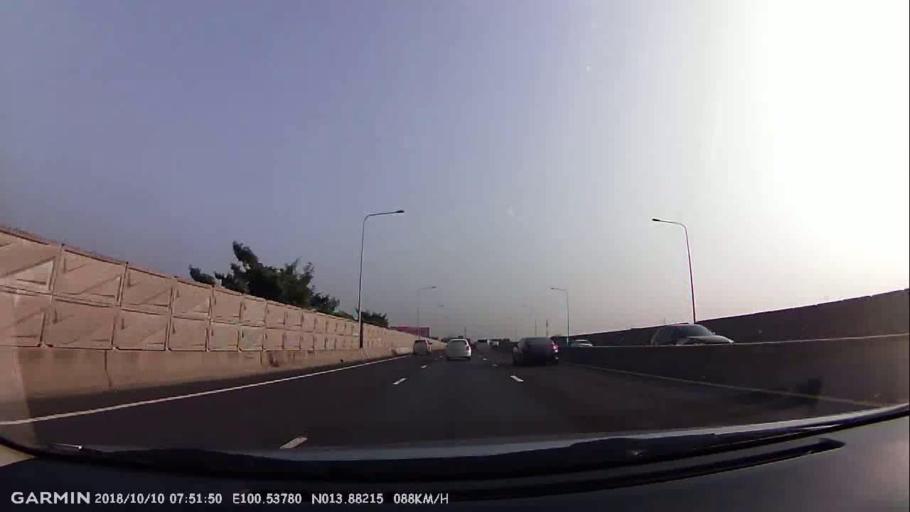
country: TH
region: Nonthaburi
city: Mueang Nonthaburi
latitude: 13.8821
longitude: 100.5374
